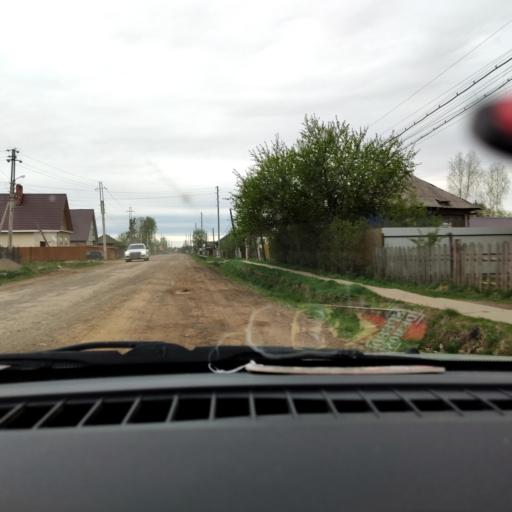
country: RU
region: Perm
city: Kudymkar
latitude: 59.0116
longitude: 54.6330
